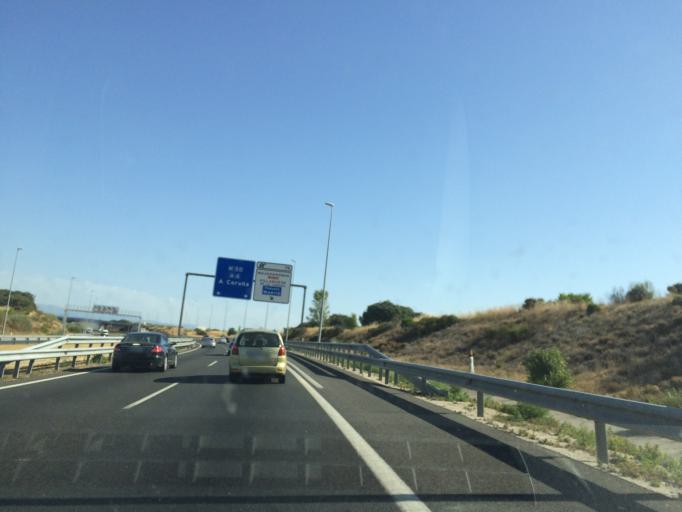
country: ES
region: Madrid
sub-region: Provincia de Madrid
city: Boadilla del Monte
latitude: 40.4382
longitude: -3.8776
